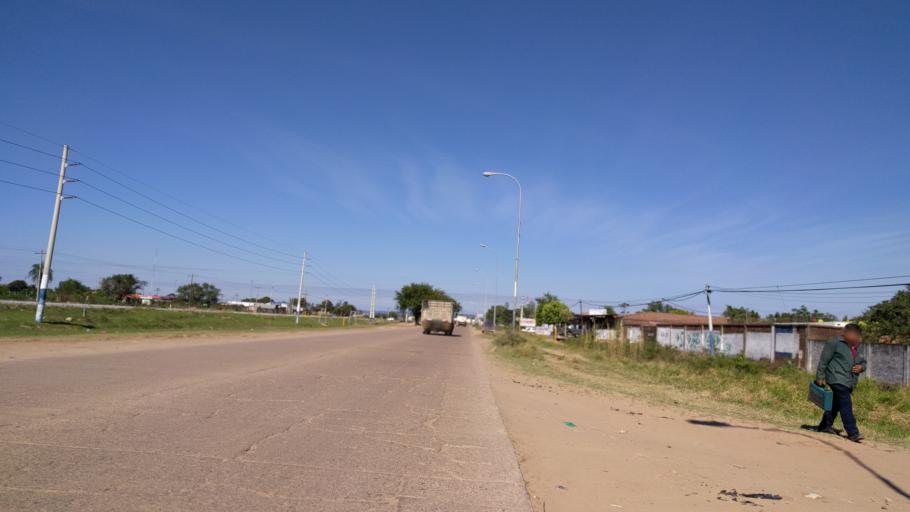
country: BO
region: Santa Cruz
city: Santa Cruz de la Sierra
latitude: -17.8704
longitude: -63.1915
